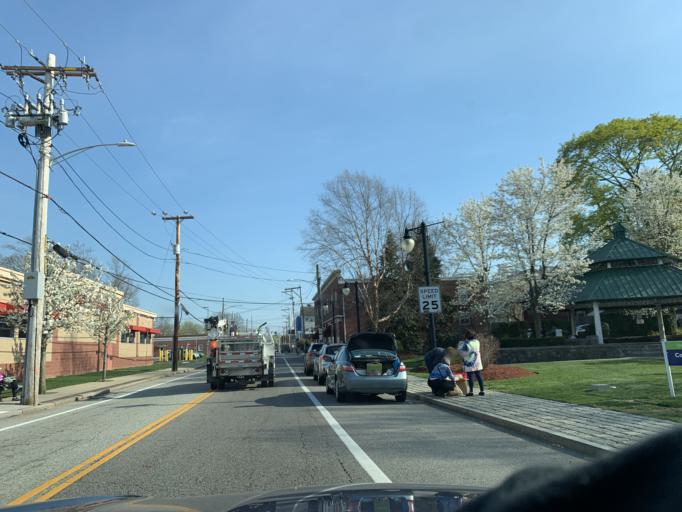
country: US
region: Rhode Island
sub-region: Kent County
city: West Warwick
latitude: 41.7041
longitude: -71.5243
